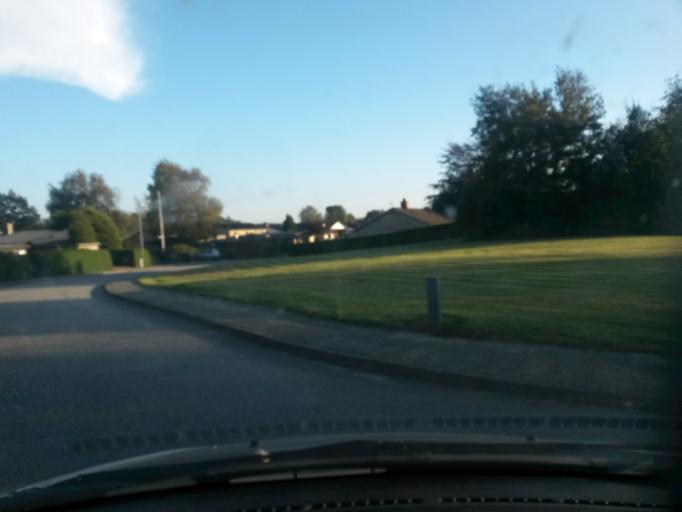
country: DK
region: Central Jutland
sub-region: Silkeborg Kommune
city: Kjellerup
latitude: 56.2759
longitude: 9.3170
